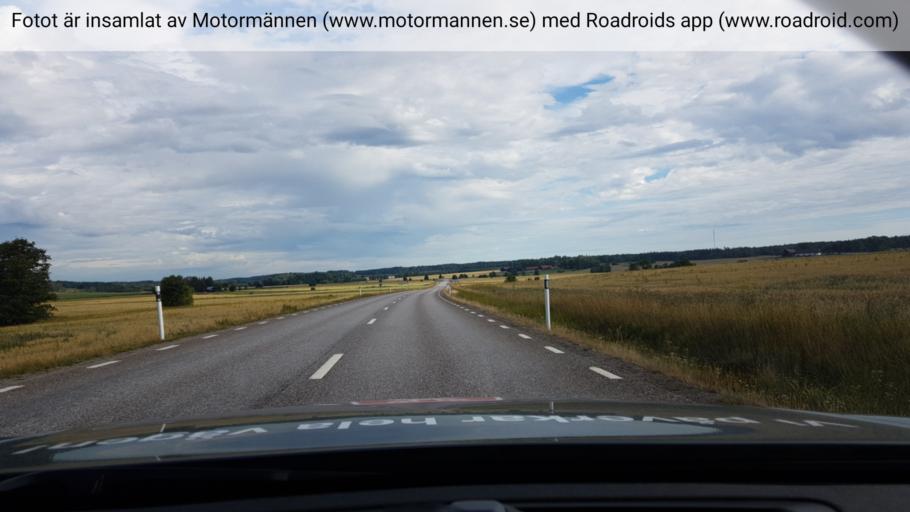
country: SE
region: Uppsala
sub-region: Heby Kommun
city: Morgongava
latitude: 59.8194
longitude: 16.9223
